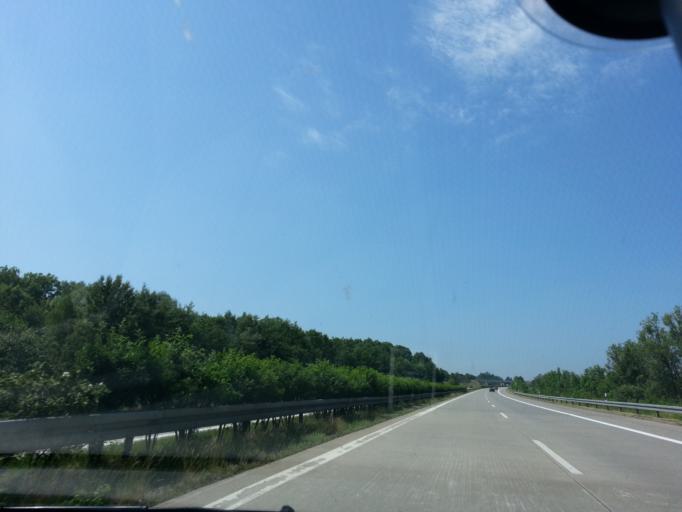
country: DE
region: Mecklenburg-Vorpommern
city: Siggelkow
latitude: 53.3086
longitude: 11.9113
